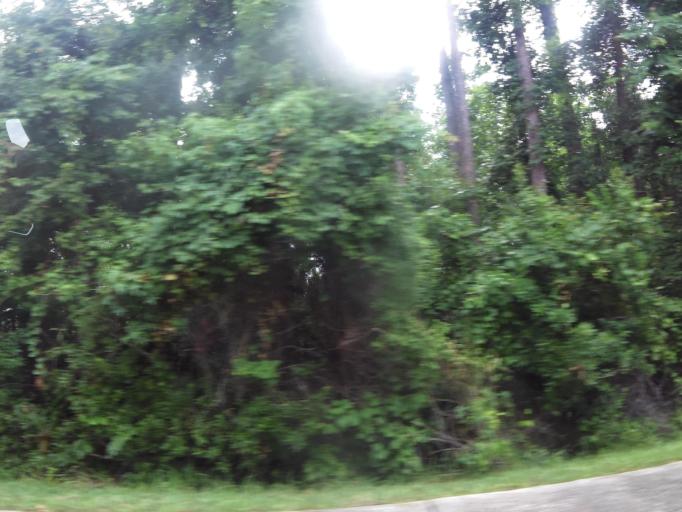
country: US
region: Florida
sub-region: Duval County
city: Jacksonville Beach
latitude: 30.2604
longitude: -81.4554
